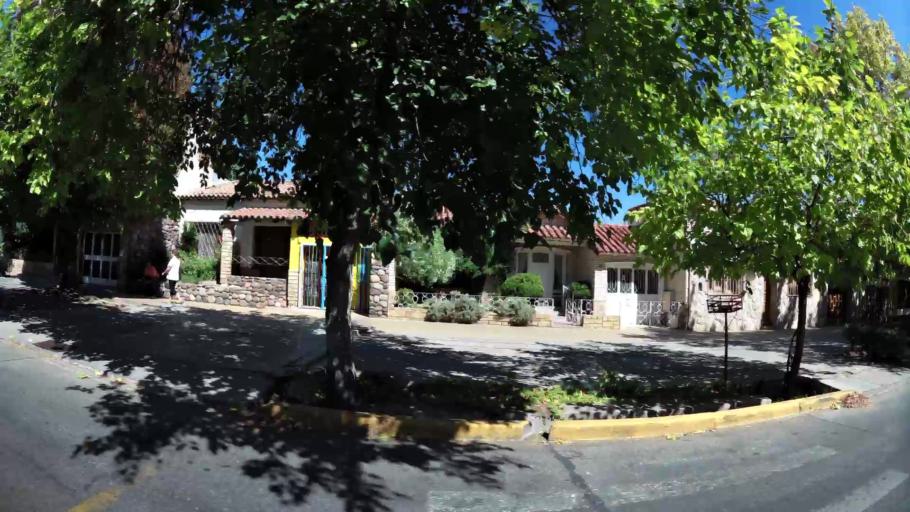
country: AR
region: Mendoza
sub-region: Departamento de Godoy Cruz
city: Godoy Cruz
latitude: -32.9156
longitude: -68.8595
